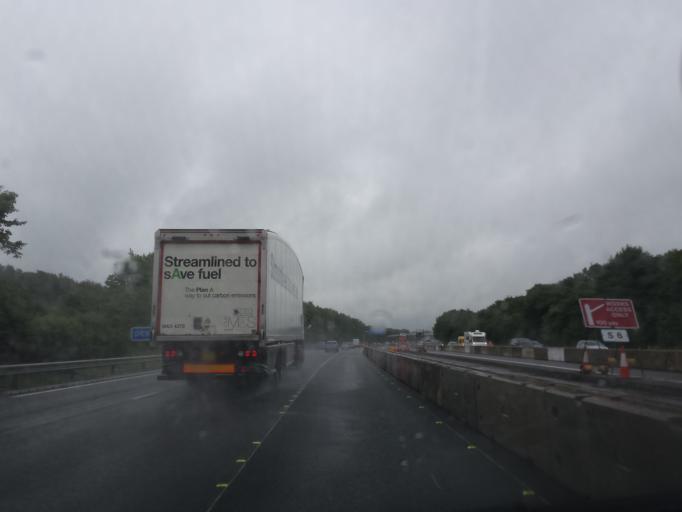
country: GB
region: England
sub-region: Rotherham
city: Harthill
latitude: 53.3089
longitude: -1.2841
